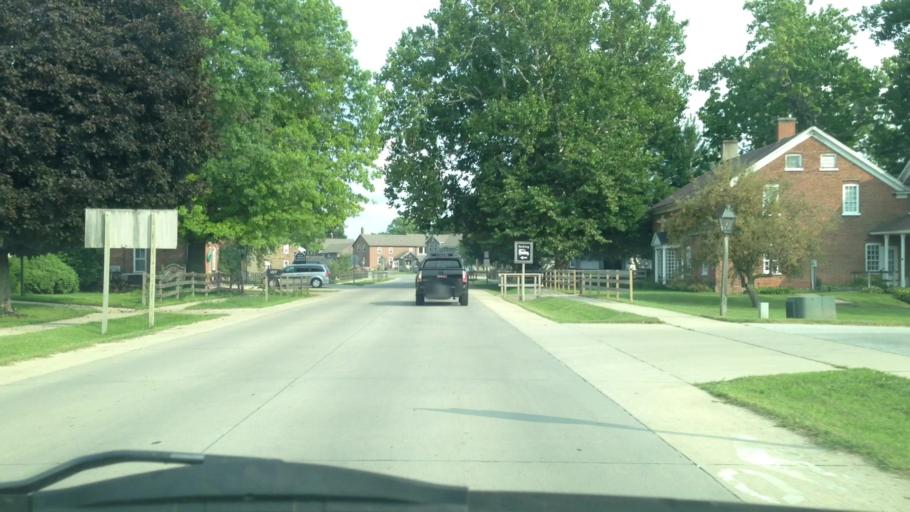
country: US
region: Iowa
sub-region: Benton County
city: Walford
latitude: 41.8011
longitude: -91.8738
